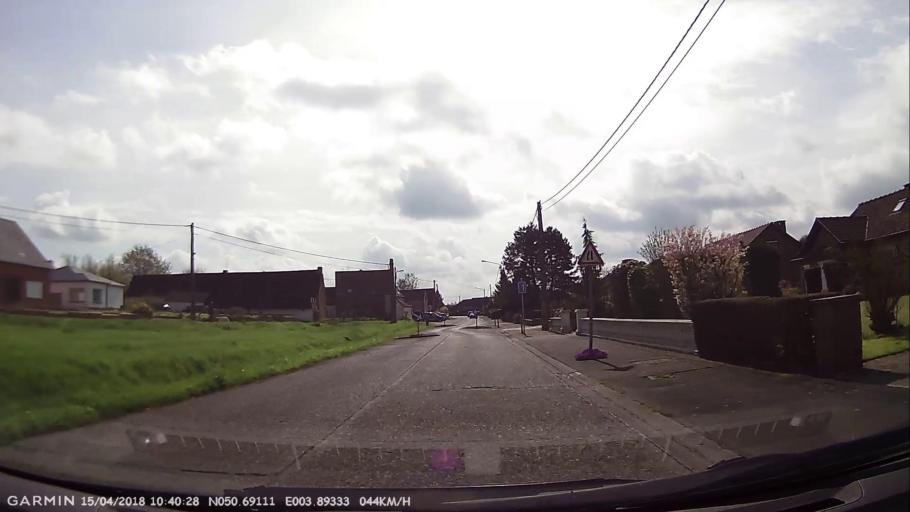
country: BE
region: Wallonia
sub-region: Province du Hainaut
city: Silly
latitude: 50.6911
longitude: 3.8934
